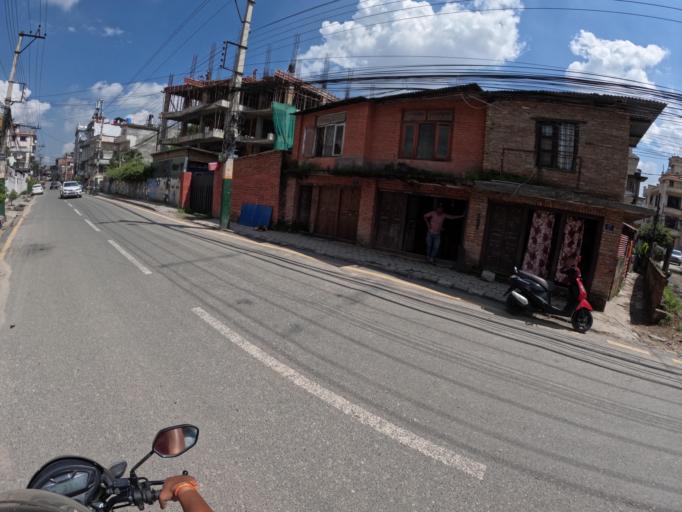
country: NP
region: Central Region
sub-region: Bagmati Zone
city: Patan
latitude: 27.6875
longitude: 85.3108
